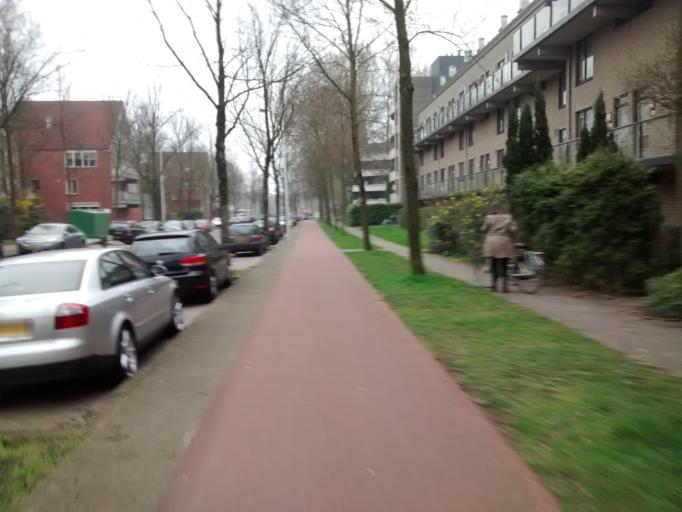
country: NL
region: Utrecht
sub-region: Gemeente Utrecht
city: Lunetten
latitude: 52.0641
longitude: 5.1395
